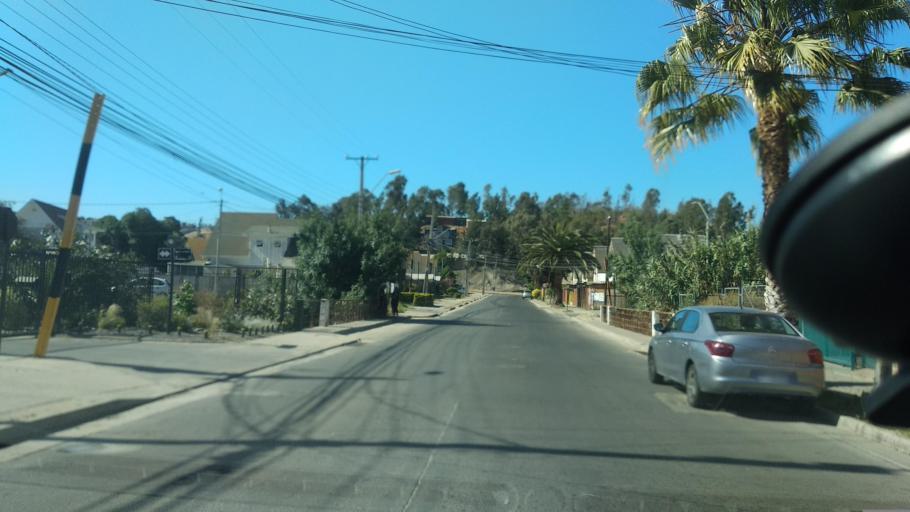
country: CL
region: Valparaiso
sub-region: Provincia de Marga Marga
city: Villa Alemana
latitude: -33.0404
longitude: -71.3904
